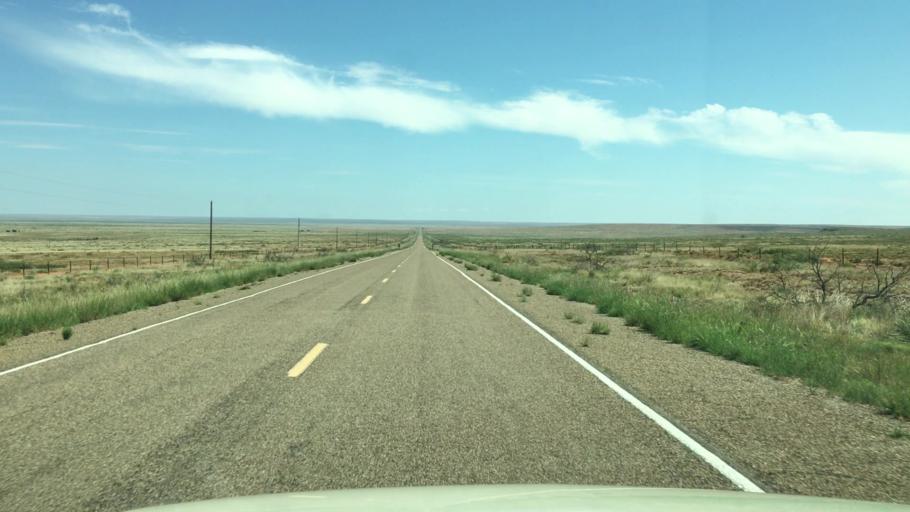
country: US
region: New Mexico
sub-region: Chaves County
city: Roswell
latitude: 33.9802
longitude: -104.5751
